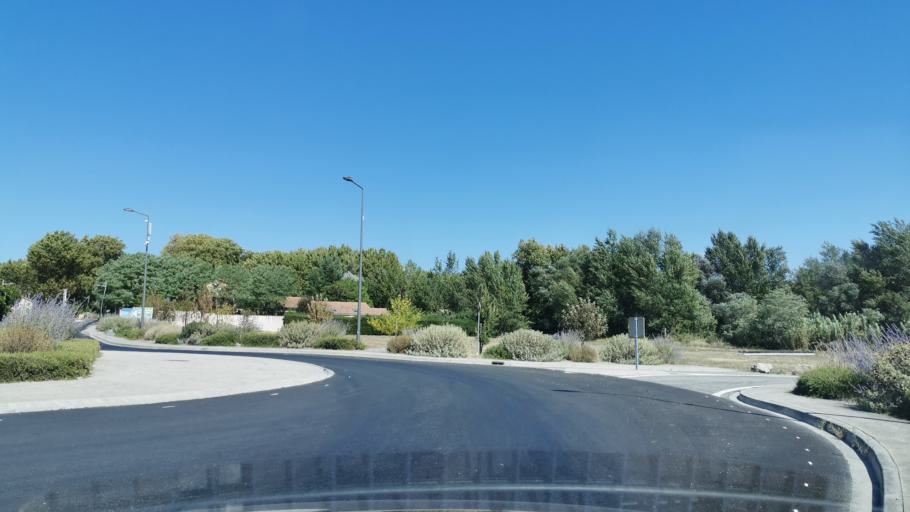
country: FR
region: Languedoc-Roussillon
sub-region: Departement de l'Aude
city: Conques-sur-Orbiel
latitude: 43.2817
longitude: 2.4372
